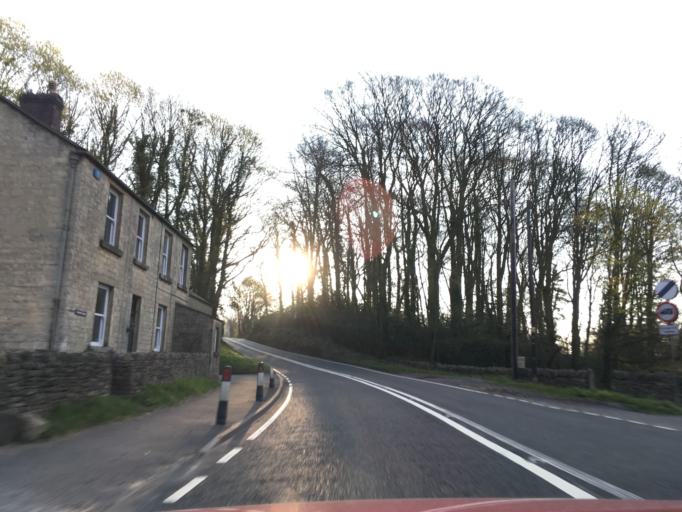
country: GB
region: England
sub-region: Gloucestershire
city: Shurdington
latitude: 51.8466
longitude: -2.0774
